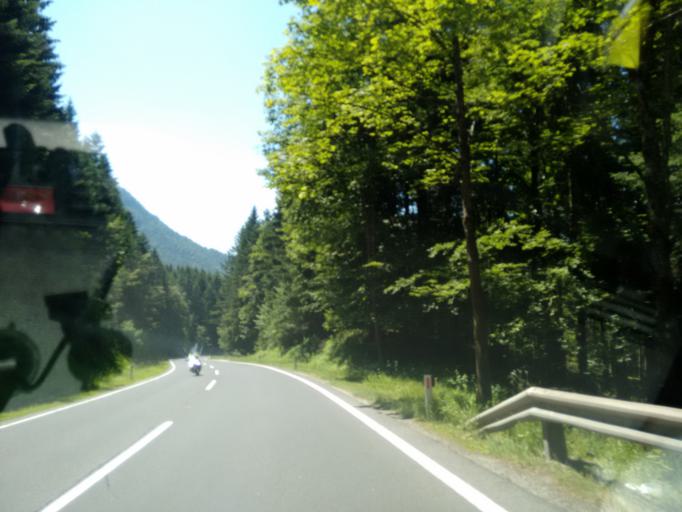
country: AT
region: Upper Austria
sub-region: Politischer Bezirk Gmunden
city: Bad Goisern
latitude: 47.6274
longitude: 13.6883
